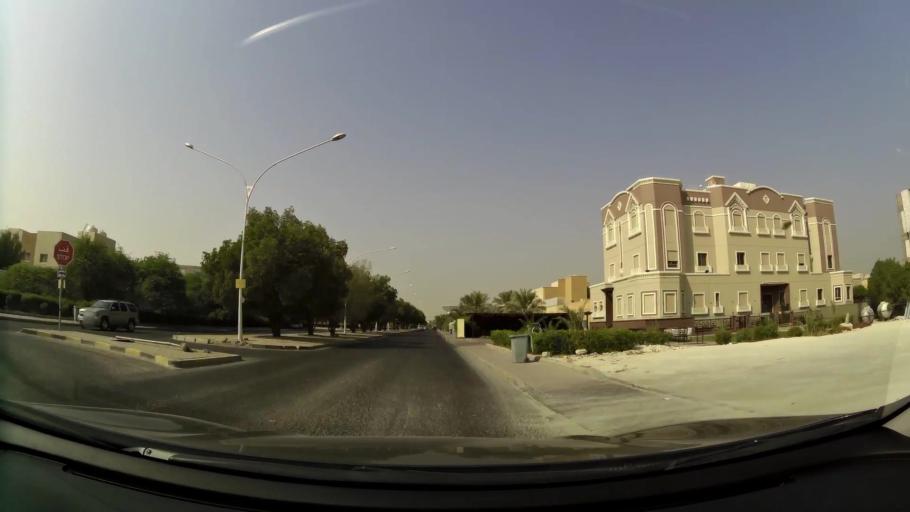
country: KW
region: Al Asimah
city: Ar Rabiyah
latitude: 29.2896
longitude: 47.8914
